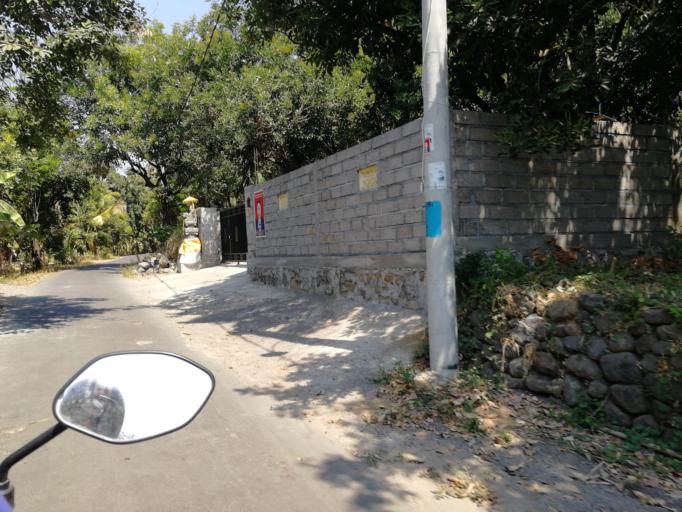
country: ID
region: Bali
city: Banjar Trunyan
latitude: -8.1264
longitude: 115.3300
